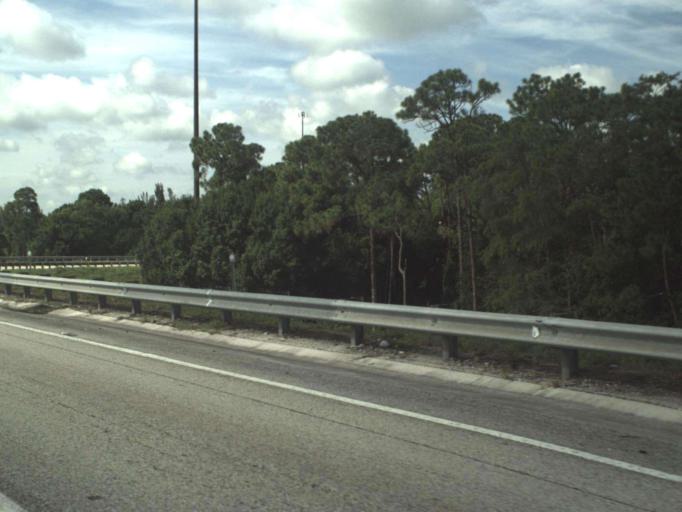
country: US
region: Florida
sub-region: Palm Beach County
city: Limestone Creek
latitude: 26.9341
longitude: -80.1503
